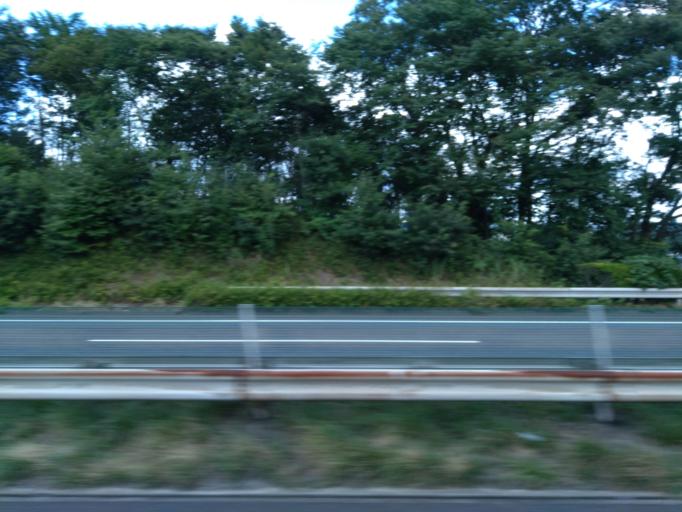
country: JP
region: Miyagi
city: Sendai-shi
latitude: 38.3147
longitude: 140.8201
